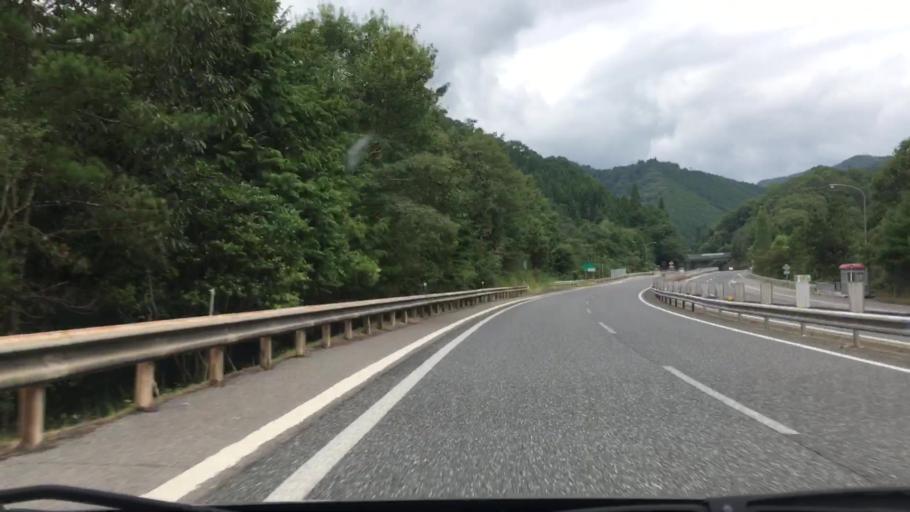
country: JP
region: Okayama
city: Niimi
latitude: 35.0100
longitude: 133.5020
